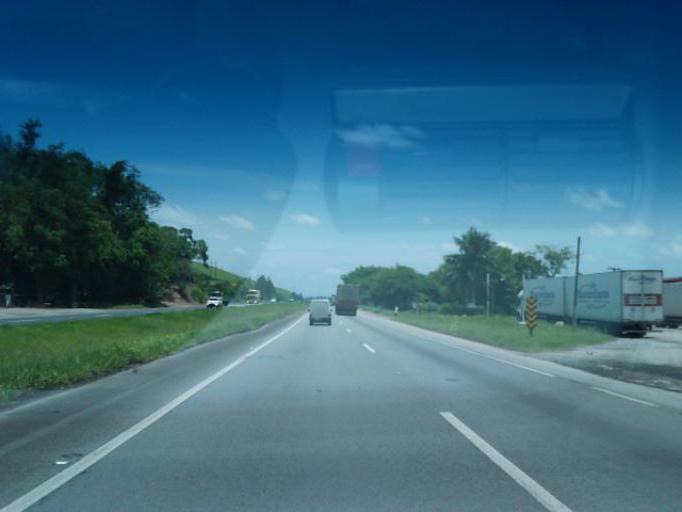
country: BR
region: Sao Paulo
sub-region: Juquia
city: Juquia
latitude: -24.3245
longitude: -47.5541
